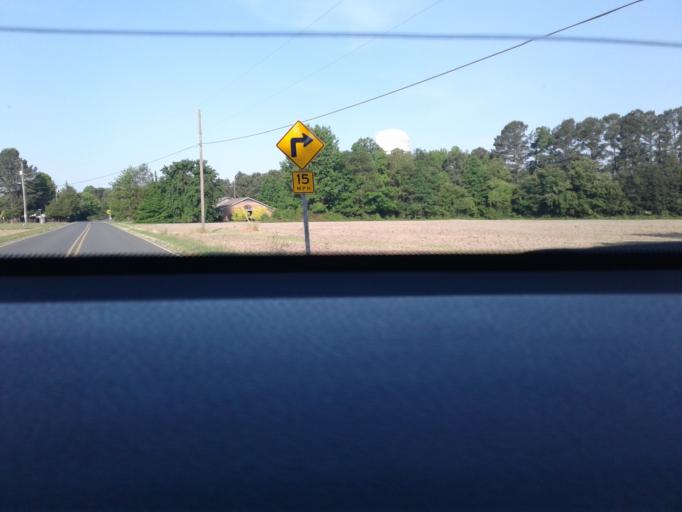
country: US
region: North Carolina
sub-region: Harnett County
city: Dunn
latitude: 35.3434
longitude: -78.5785
